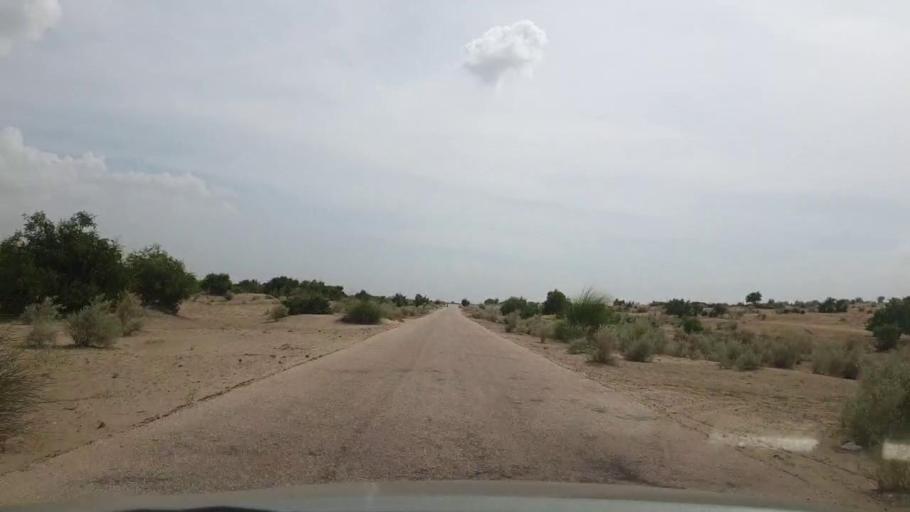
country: PK
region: Sindh
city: Kot Diji
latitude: 27.1529
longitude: 69.0340
